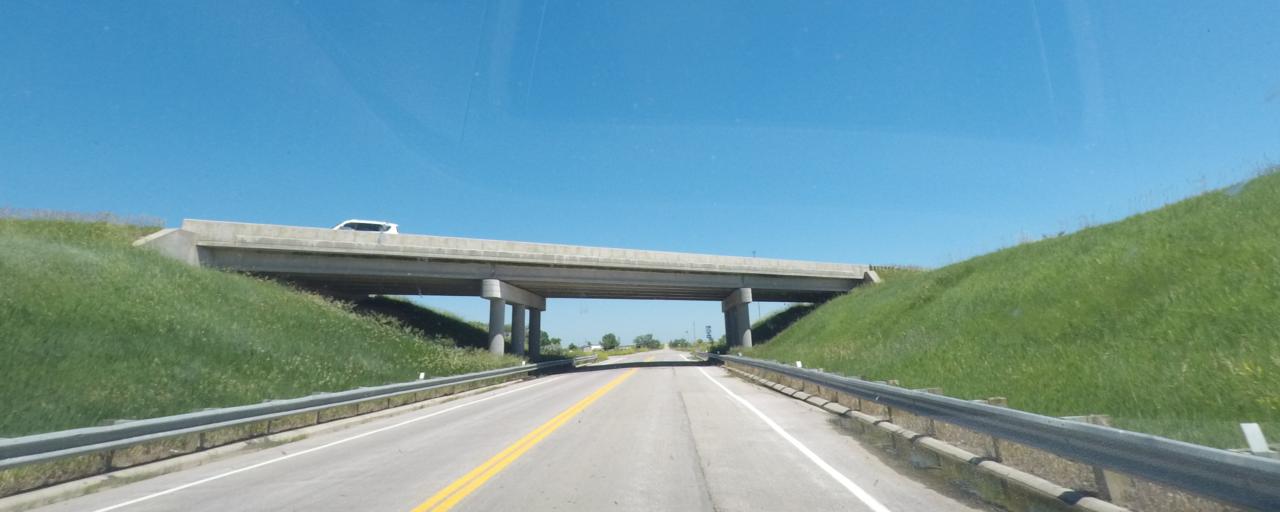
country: US
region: South Dakota
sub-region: Haakon County
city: Philip
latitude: 43.9366
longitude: -102.1519
